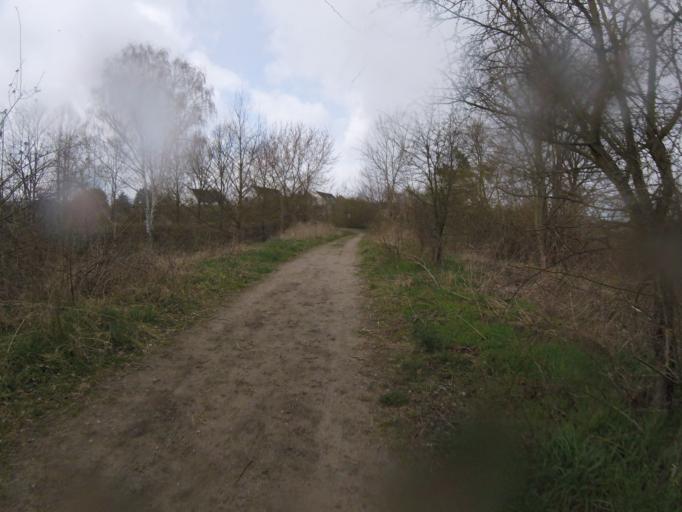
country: DE
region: Brandenburg
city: Schwerin
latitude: 52.2019
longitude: 13.5878
